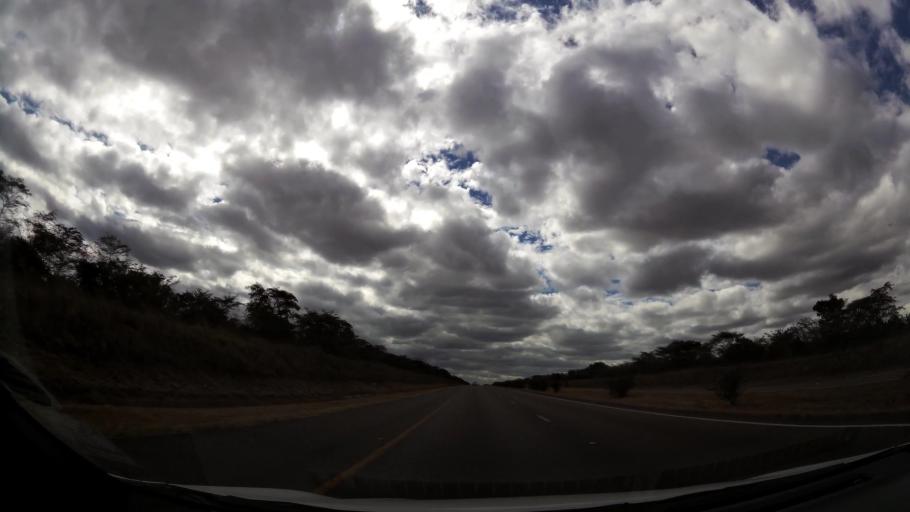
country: ZA
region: Limpopo
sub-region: Waterberg District Municipality
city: Bela-Bela
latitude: -24.8655
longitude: 28.3914
